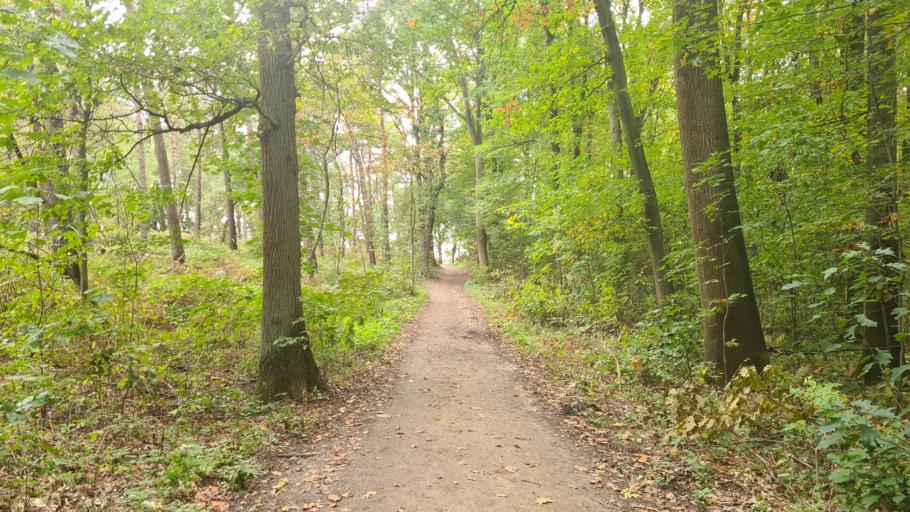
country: DE
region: North Rhine-Westphalia
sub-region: Regierungsbezirk Munster
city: Recklinghausen
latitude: 51.6749
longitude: 7.1838
